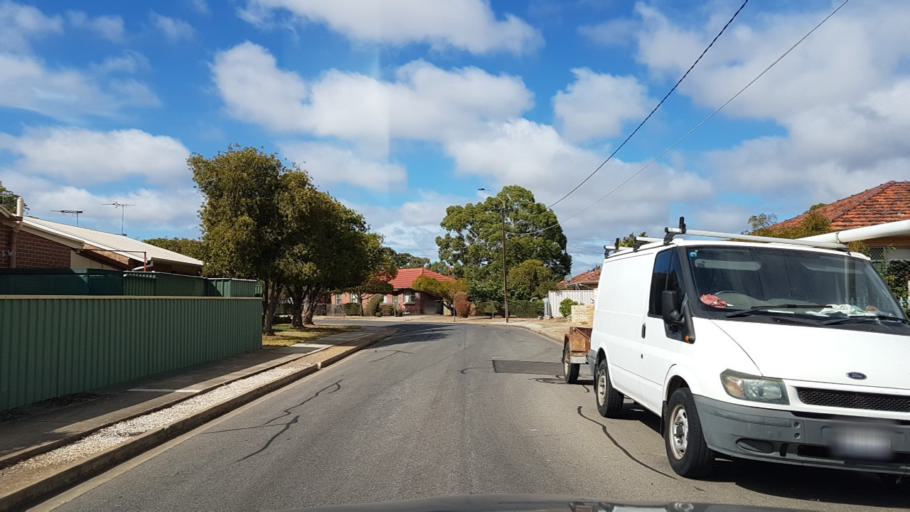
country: AU
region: South Australia
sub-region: Marion
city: Plympton Park
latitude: -34.9829
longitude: 138.5472
